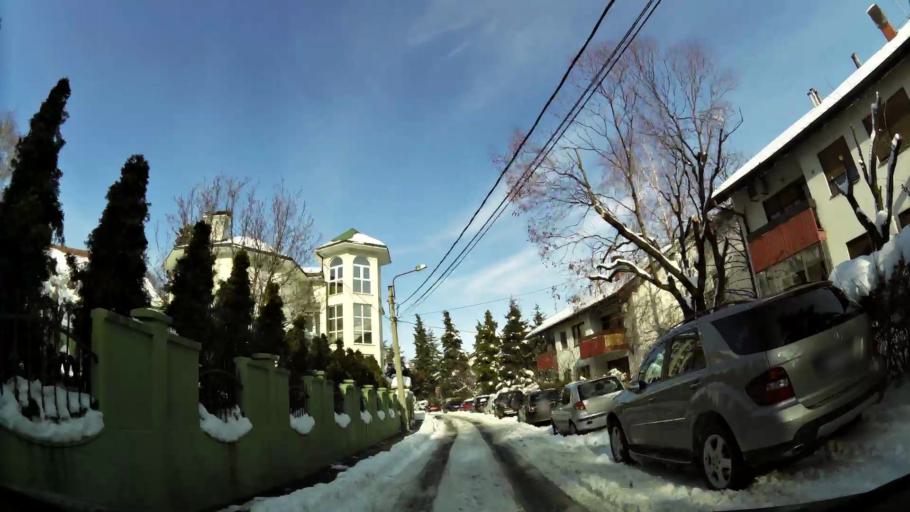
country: RS
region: Central Serbia
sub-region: Belgrade
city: Palilula
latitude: 44.8039
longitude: 20.5203
